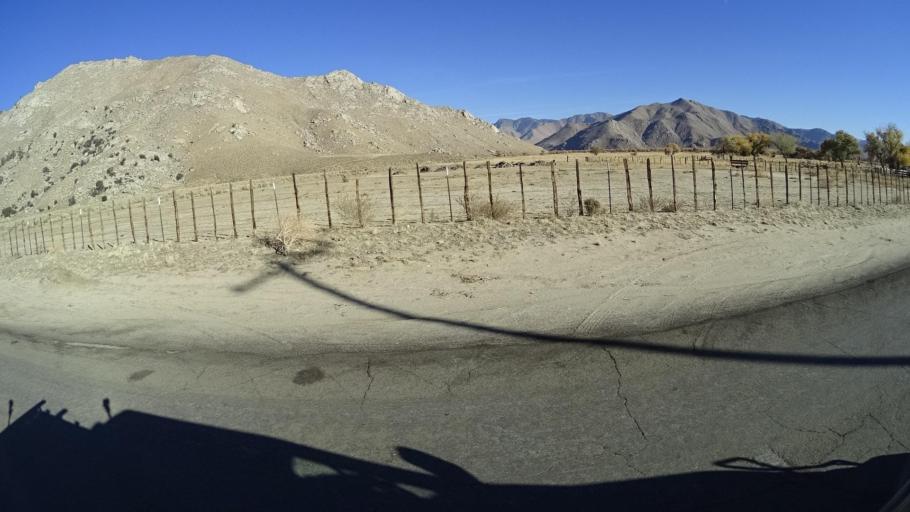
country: US
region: California
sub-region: Kern County
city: Weldon
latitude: 35.6901
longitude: -118.2901
